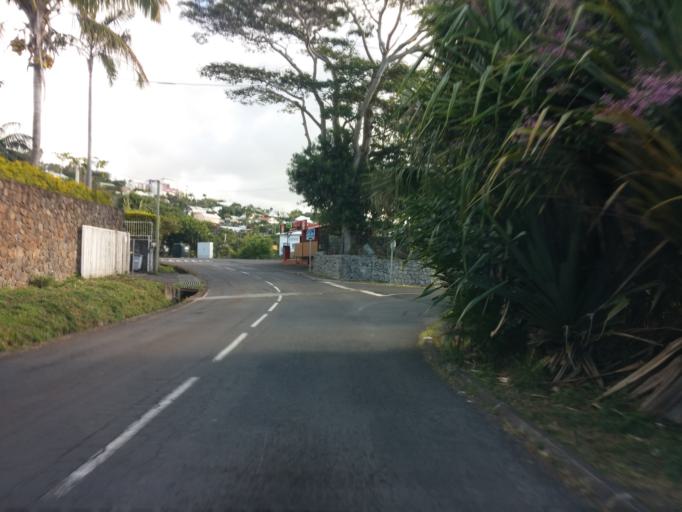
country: RE
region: Reunion
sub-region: Reunion
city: Saint-Denis
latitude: -20.8836
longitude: 55.4274
